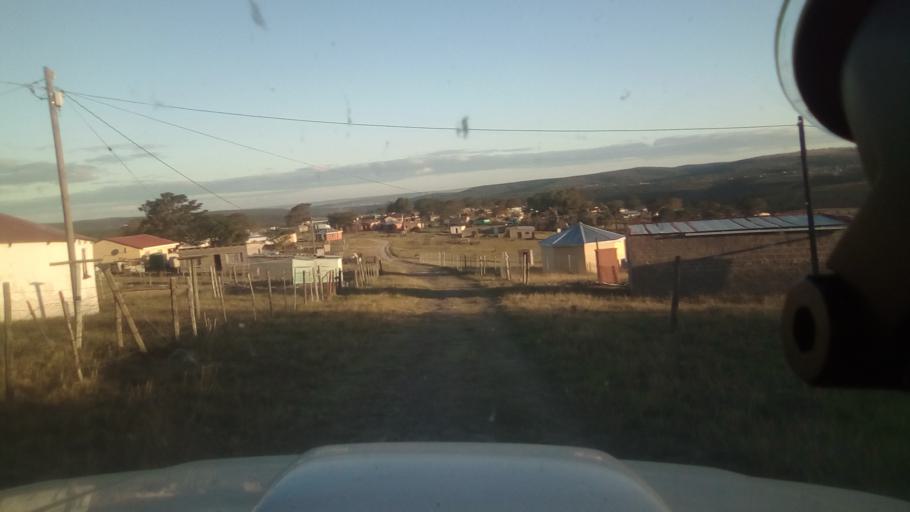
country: ZA
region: Eastern Cape
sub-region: Buffalo City Metropolitan Municipality
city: Bhisho
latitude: -32.7335
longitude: 27.3779
